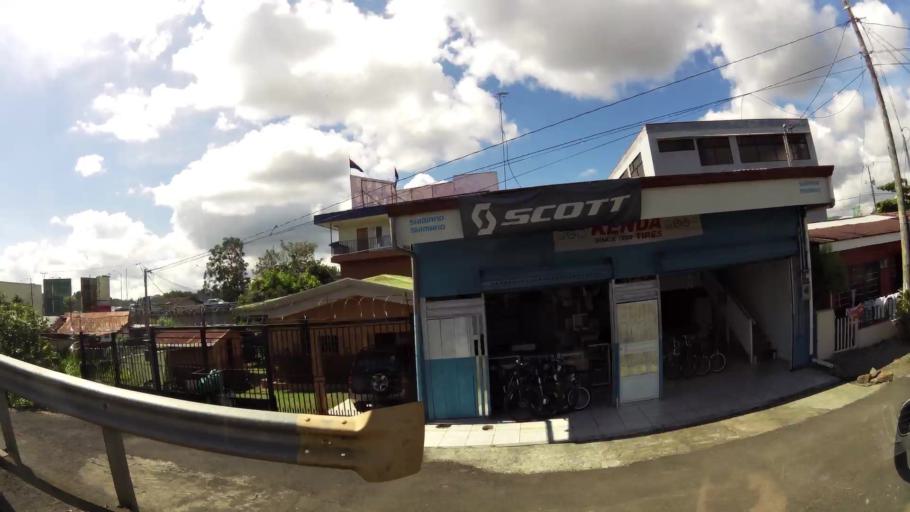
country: CR
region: San Jose
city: San Isidro
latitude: 9.3729
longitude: -83.7005
